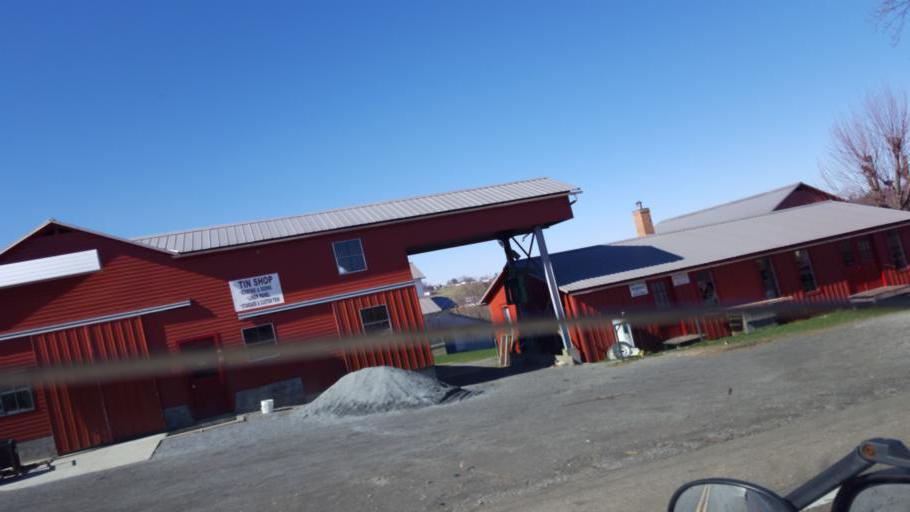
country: US
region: Ohio
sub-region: Wayne County
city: Apple Creek
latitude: 40.6650
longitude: -81.7451
